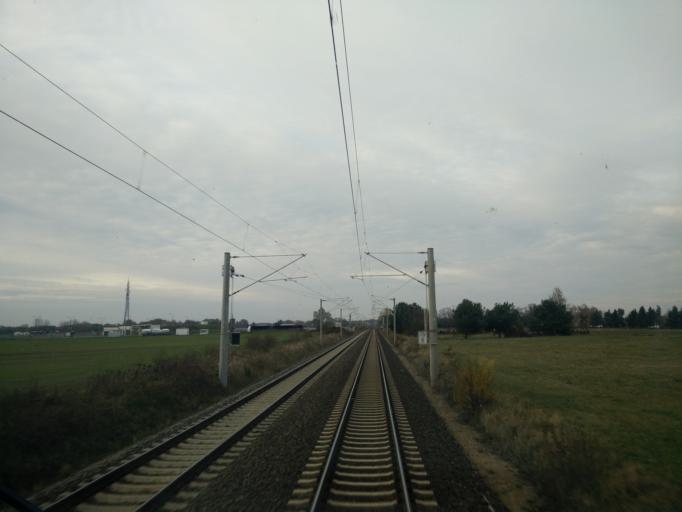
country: DE
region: Brandenburg
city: Luebben
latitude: 51.9233
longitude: 13.8934
